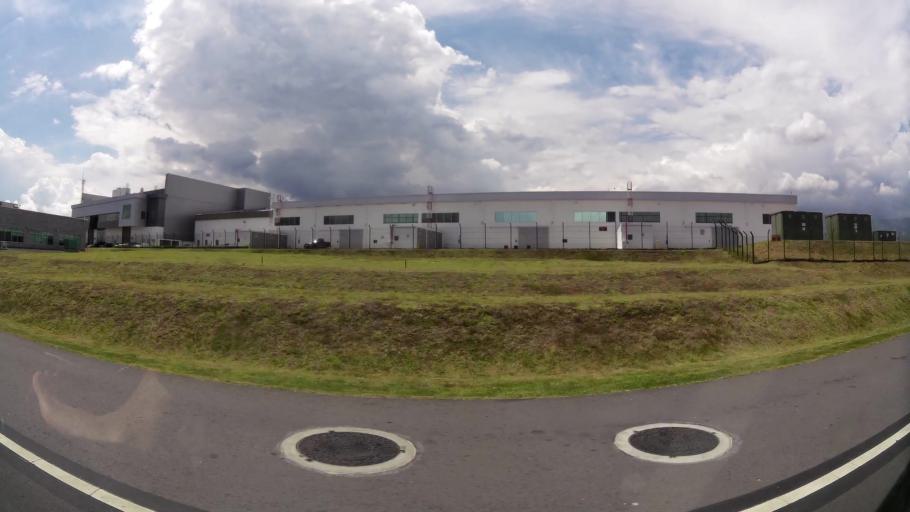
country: EC
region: Pichincha
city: Quito
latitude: -0.1395
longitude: -78.3574
